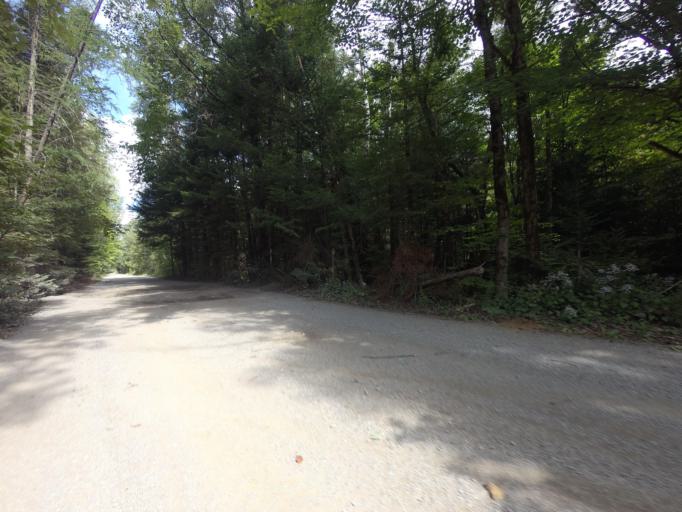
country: CA
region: Ontario
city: Omemee
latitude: 44.7471
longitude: -78.6658
